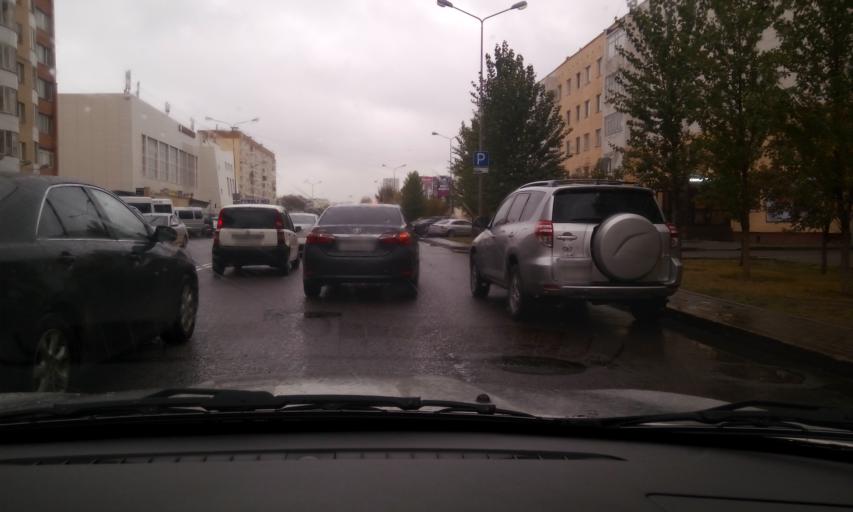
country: KZ
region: Astana Qalasy
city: Astana
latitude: 51.1691
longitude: 71.4052
